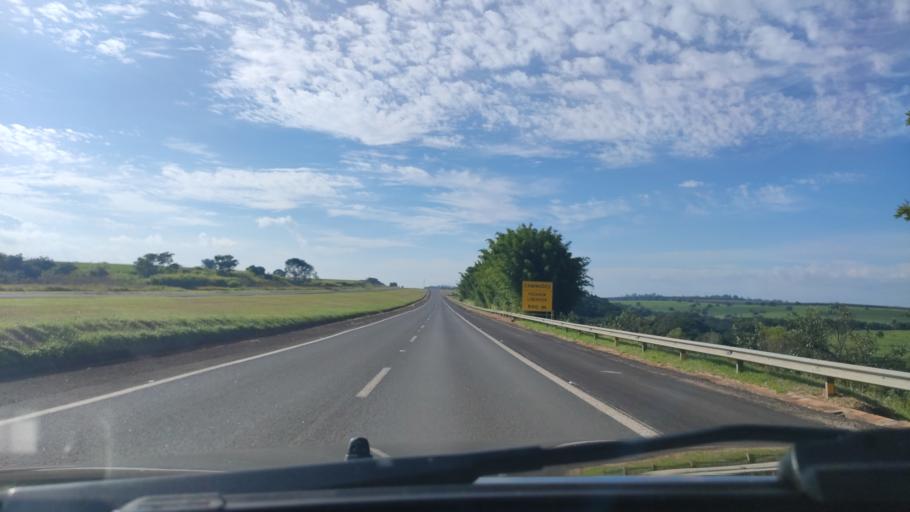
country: BR
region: Sao Paulo
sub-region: Itatinga
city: Itatinga
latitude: -22.9854
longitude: -48.7675
